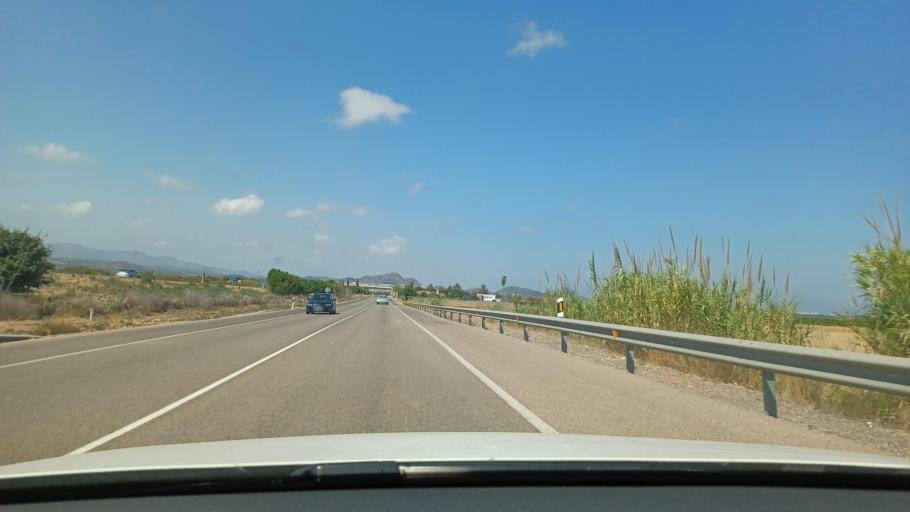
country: ES
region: Valencia
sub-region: Provincia de Valencia
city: Faura
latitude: 39.7075
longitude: -0.2556
